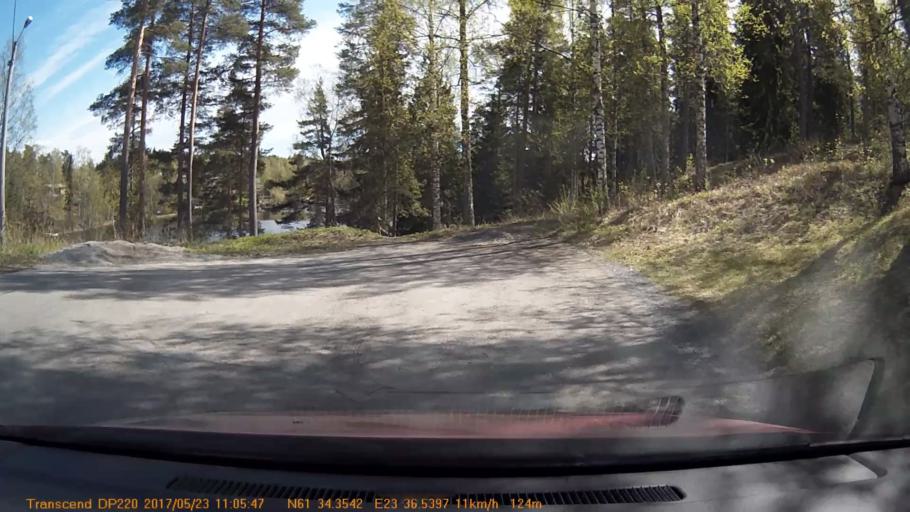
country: FI
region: Pirkanmaa
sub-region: Tampere
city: Yloejaervi
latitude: 61.5726
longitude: 23.6089
